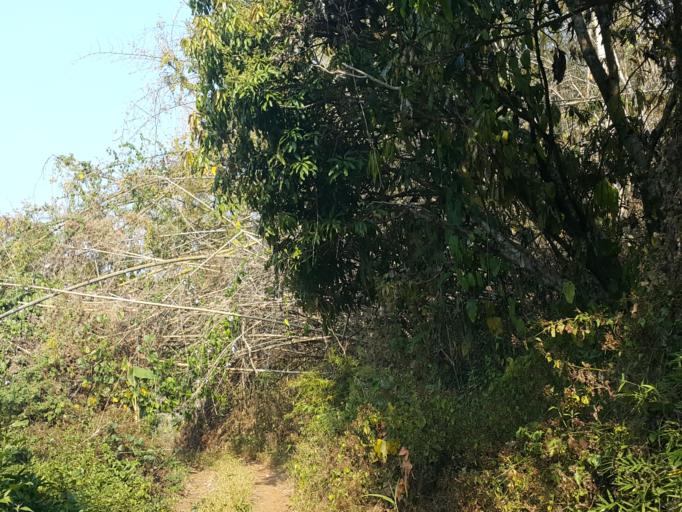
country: TH
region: Chiang Mai
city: Hang Dong
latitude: 18.7543
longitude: 98.8442
